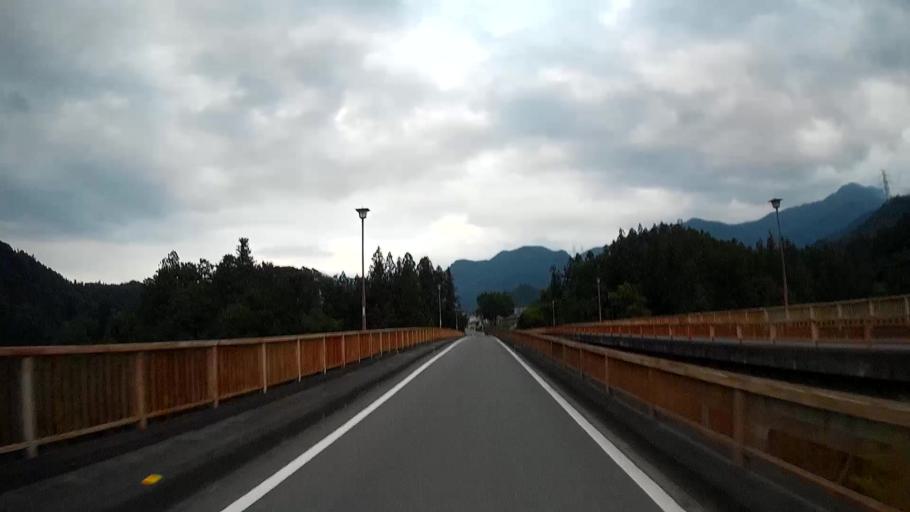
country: JP
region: Saitama
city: Chichibu
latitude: 35.9577
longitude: 139.0100
